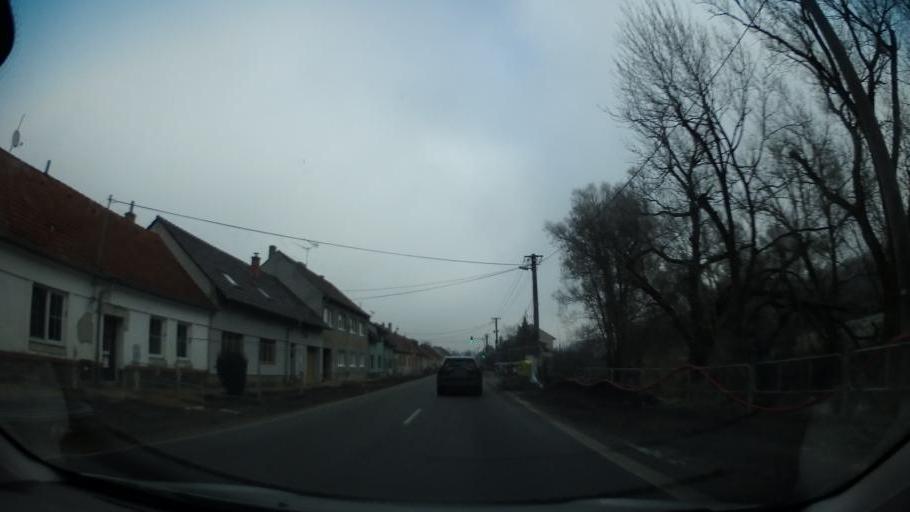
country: CZ
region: Vysocina
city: Vladislav
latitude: 49.2117
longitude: 15.9789
